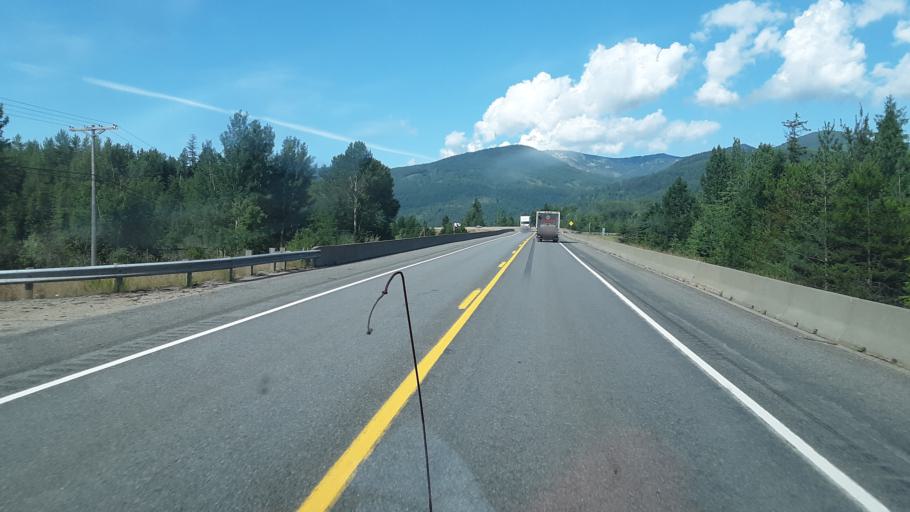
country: US
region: Idaho
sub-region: Bonner County
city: Ponderay
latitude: 48.4159
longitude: -116.5114
